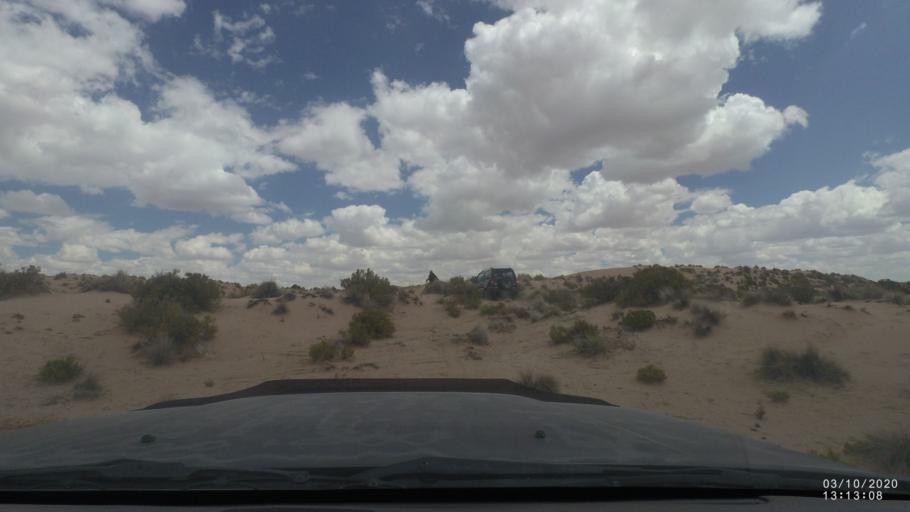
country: BO
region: Oruro
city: Poopo
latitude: -18.6907
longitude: -67.5342
